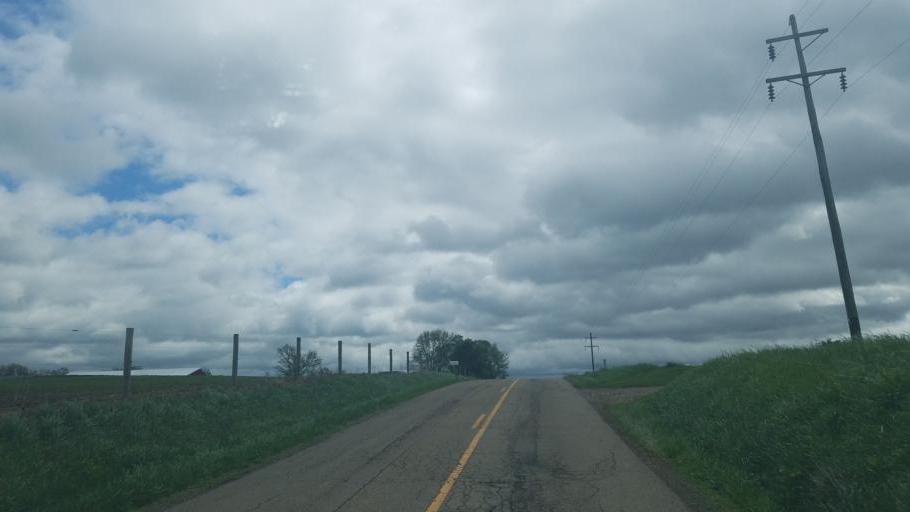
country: US
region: Ohio
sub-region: Knox County
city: Danville
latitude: 40.5363
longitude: -82.3817
